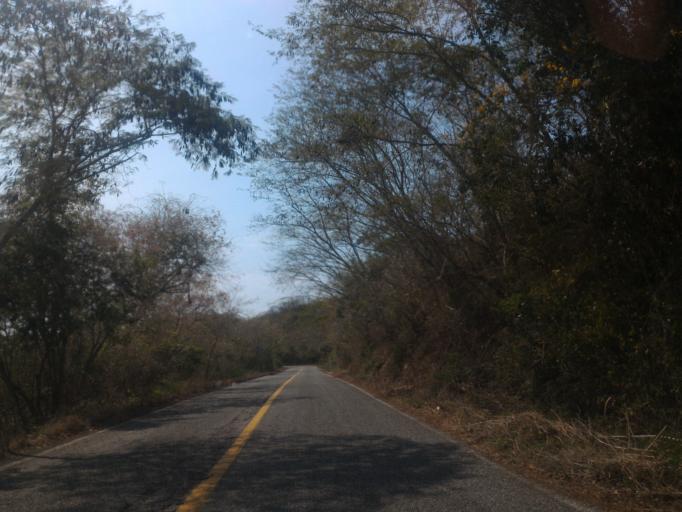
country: MX
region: Michoacan
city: Coahuayana Viejo
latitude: 18.3453
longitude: -103.4832
